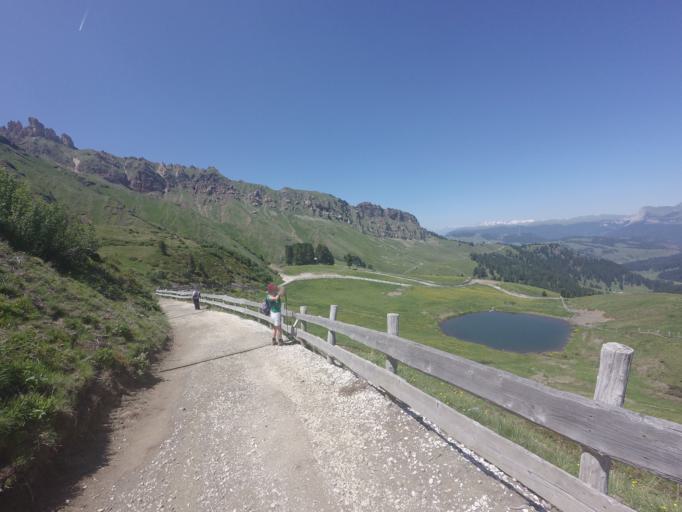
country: IT
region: Trentino-Alto Adige
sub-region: Provincia di Trento
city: Mazzin
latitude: 46.4989
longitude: 11.6521
